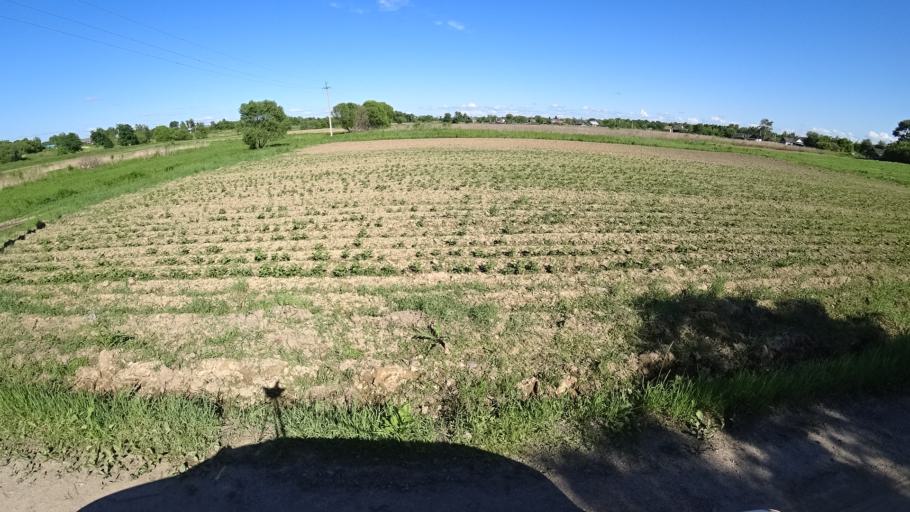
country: RU
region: Khabarovsk Krai
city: Khor
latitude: 47.8865
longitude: 135.0194
